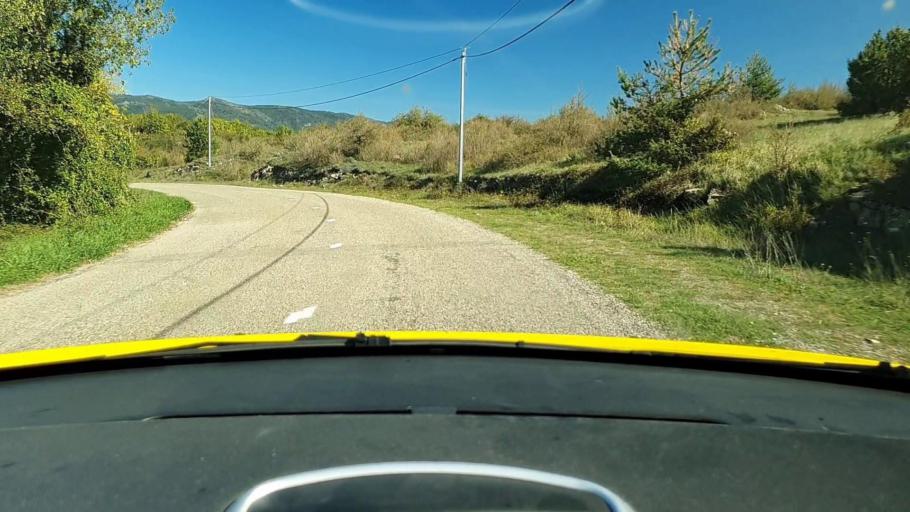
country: FR
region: Languedoc-Roussillon
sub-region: Departement du Gard
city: Aveze
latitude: 43.9615
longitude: 3.4088
